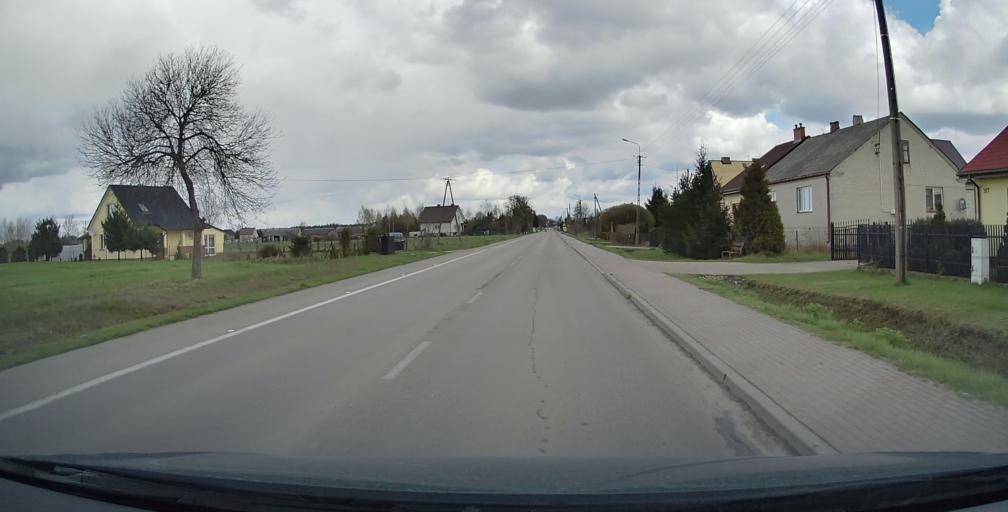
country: PL
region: Masovian Voivodeship
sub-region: Powiat ostrolecki
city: Goworowo
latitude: 52.9364
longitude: 21.5876
